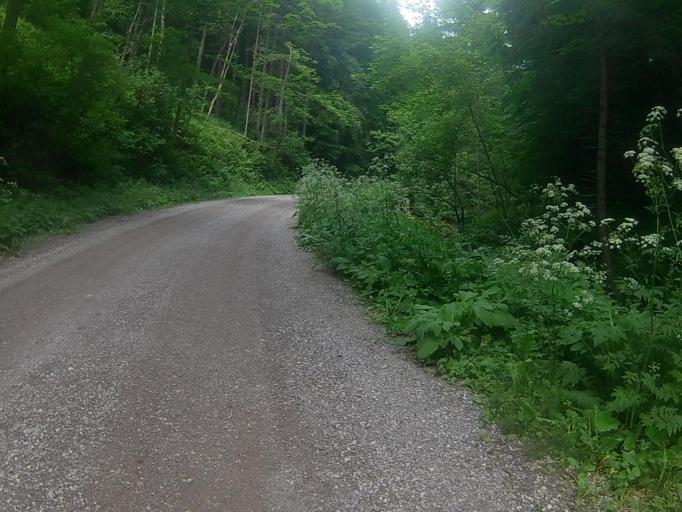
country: SI
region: Maribor
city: Bresternica
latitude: 46.6130
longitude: 15.5713
